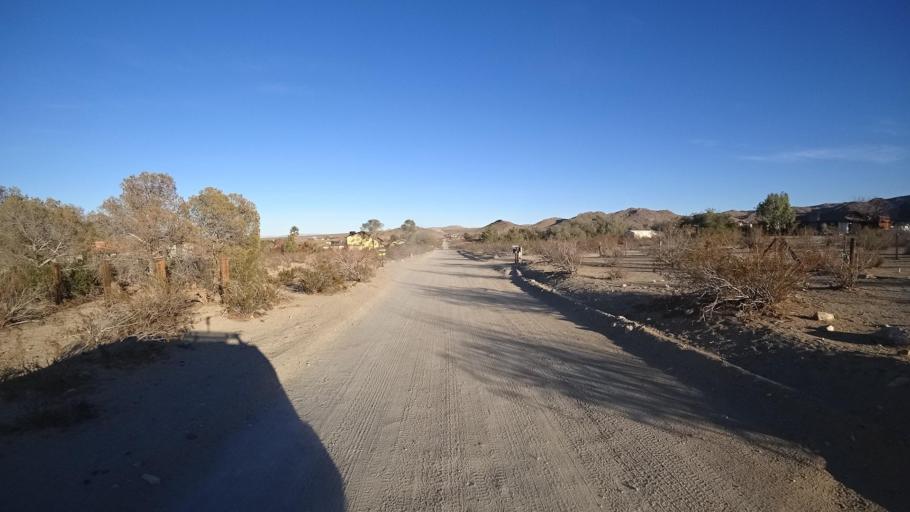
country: US
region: California
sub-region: Kern County
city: Ridgecrest
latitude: 35.5824
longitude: -117.6602
